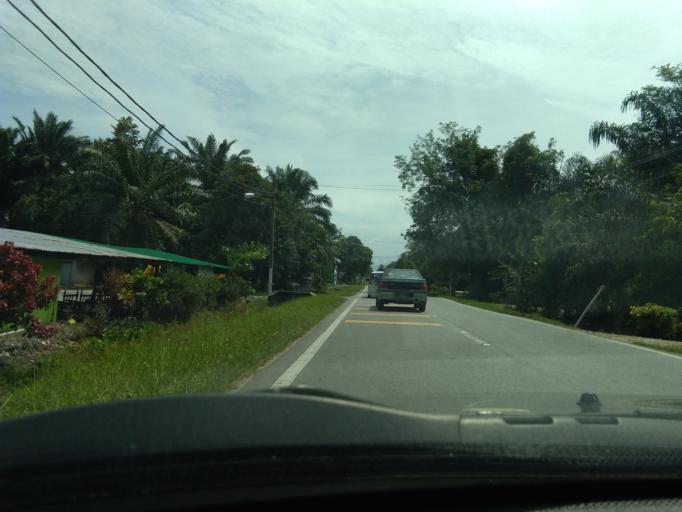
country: MY
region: Perak
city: Bagan Serai
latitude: 5.0457
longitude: 100.5802
